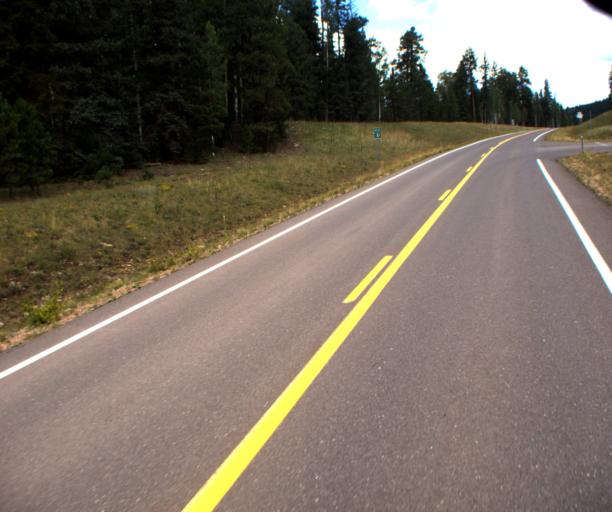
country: US
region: Arizona
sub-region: Apache County
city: Eagar
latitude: 33.9748
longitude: -109.5006
